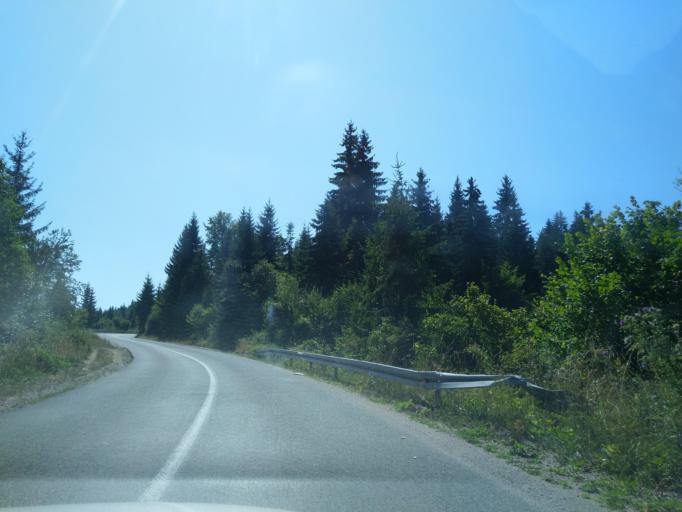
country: RS
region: Central Serbia
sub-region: Zlatiborski Okrug
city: Nova Varos
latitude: 43.4090
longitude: 19.8381
